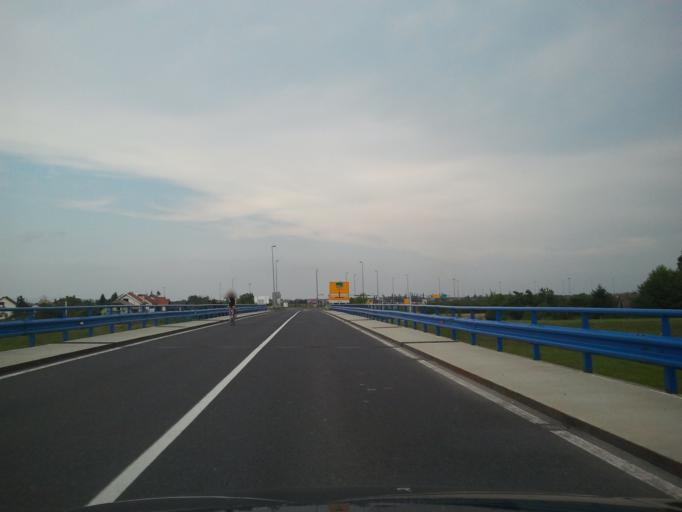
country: HR
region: Zagrebacka
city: Gradici
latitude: 45.6873
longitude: 16.0577
